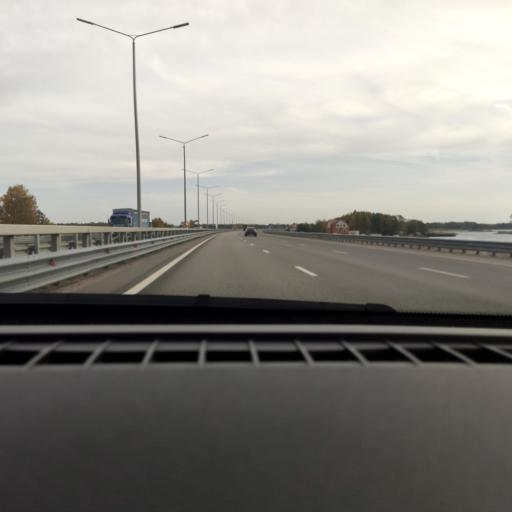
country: RU
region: Voronezj
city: Somovo
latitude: 51.7895
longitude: 39.2768
